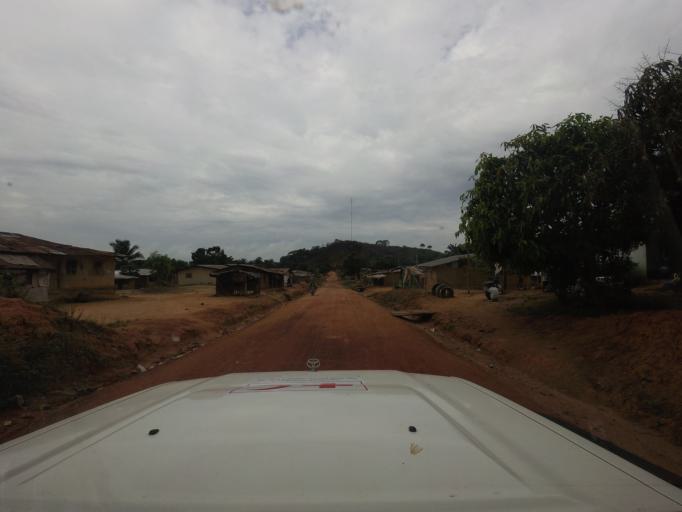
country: SL
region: Eastern Province
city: Buedu
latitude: 8.2827
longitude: -10.0910
